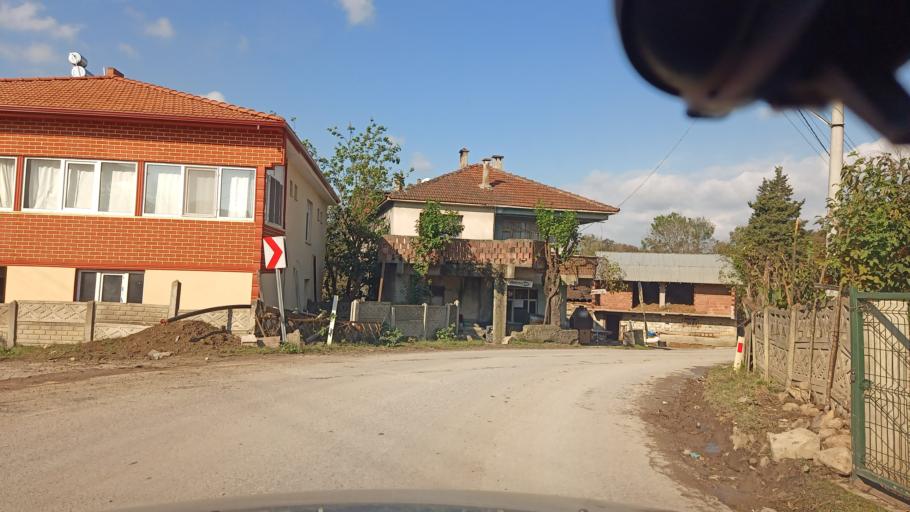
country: TR
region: Sakarya
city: Kaynarca
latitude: 41.0919
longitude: 30.4429
